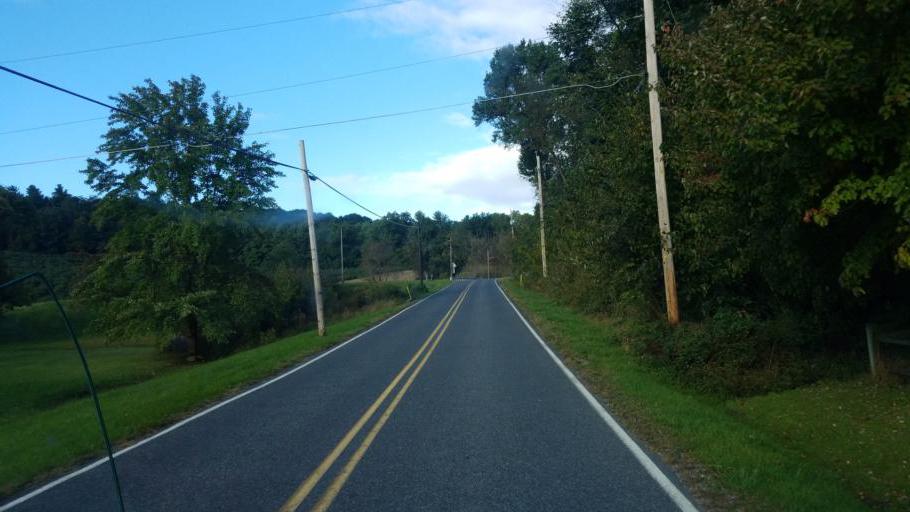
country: US
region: Pennsylvania
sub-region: Adams County
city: Biglerville
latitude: 39.8848
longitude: -77.3628
